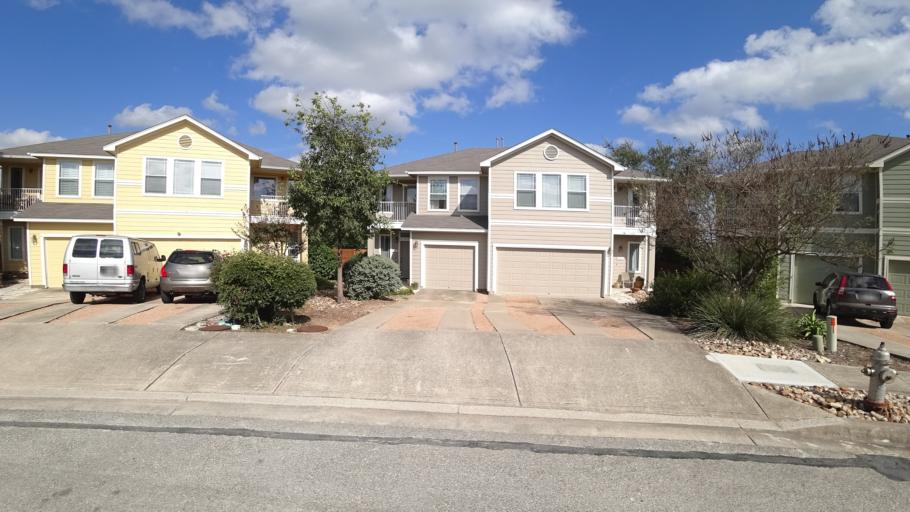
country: US
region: Texas
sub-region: Travis County
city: Barton Creek
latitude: 30.2544
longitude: -97.8958
